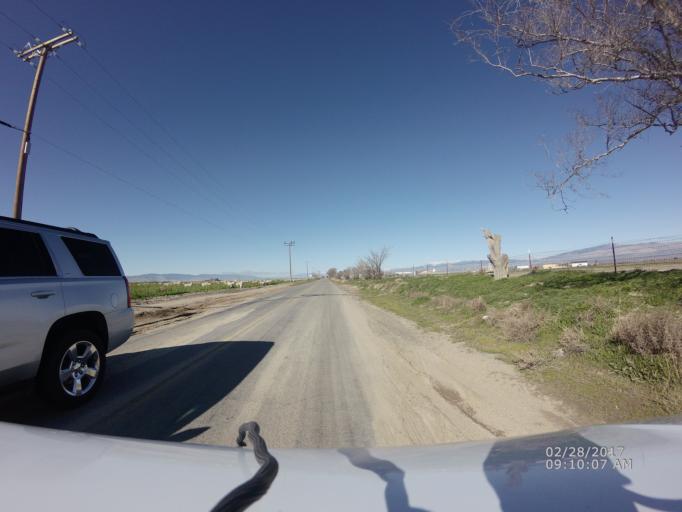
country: US
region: California
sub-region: Kern County
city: Rosamond
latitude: 34.8201
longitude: -118.2907
